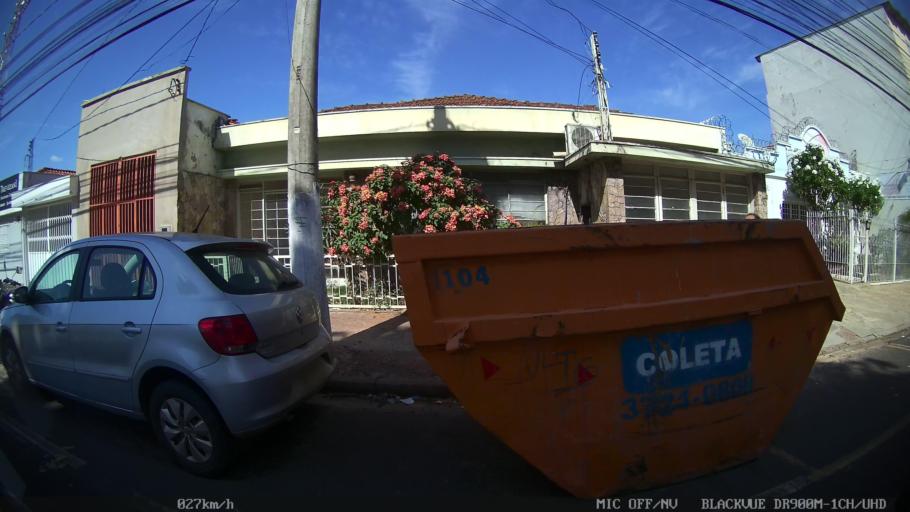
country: BR
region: Sao Paulo
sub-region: Franca
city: Franca
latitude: -20.5381
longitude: -47.4135
